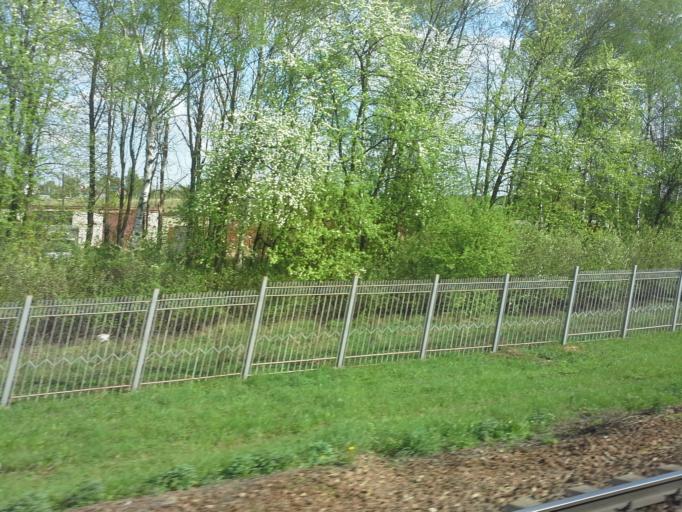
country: RU
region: Moskovskaya
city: Pravdinskiy
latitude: 56.0560
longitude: 37.8630
